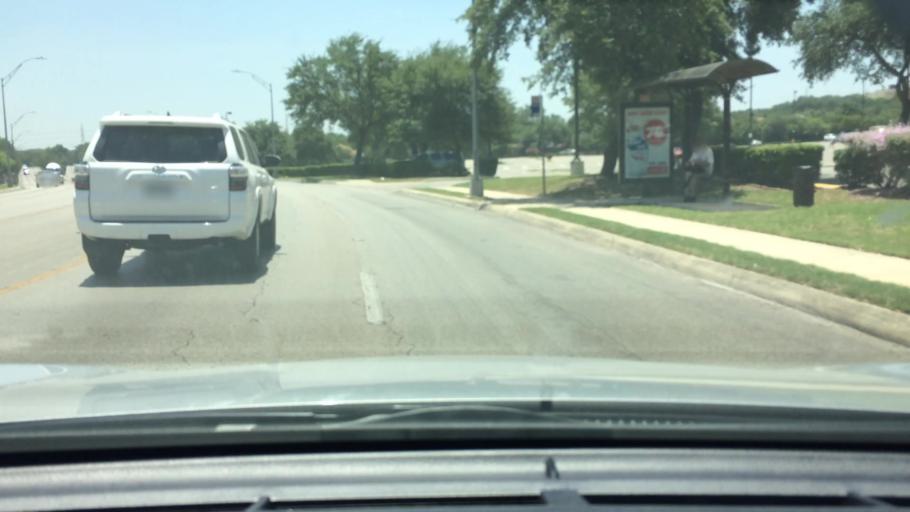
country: US
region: Texas
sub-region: Bexar County
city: Shavano Park
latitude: 29.5630
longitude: -98.5853
